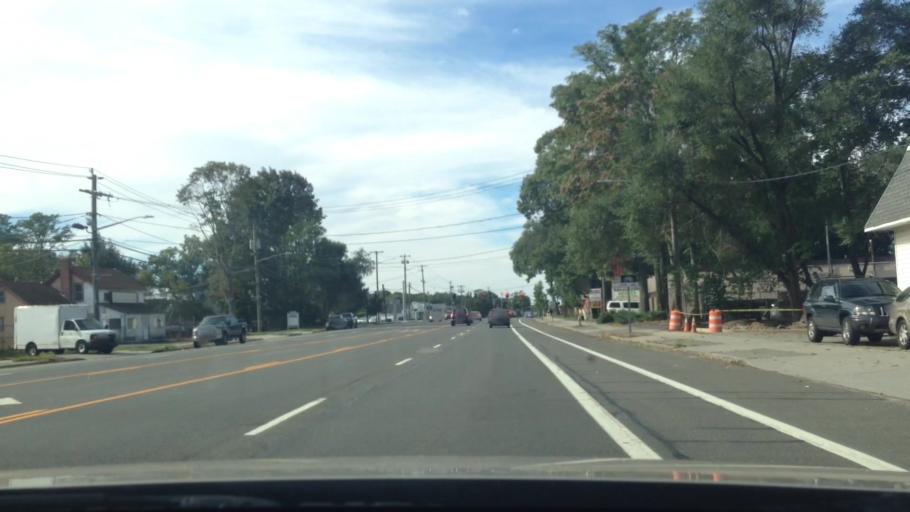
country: US
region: New York
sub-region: Suffolk County
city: Selden
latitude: 40.8646
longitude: -73.0450
